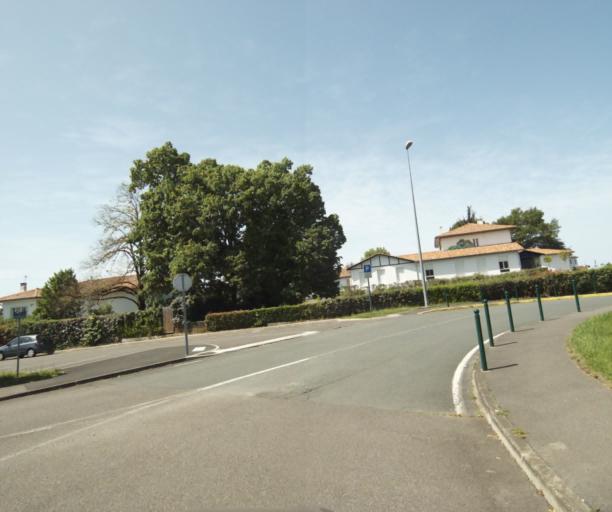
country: FR
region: Aquitaine
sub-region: Departement des Pyrenees-Atlantiques
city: Mouguerre
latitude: 43.4697
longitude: -1.4459
